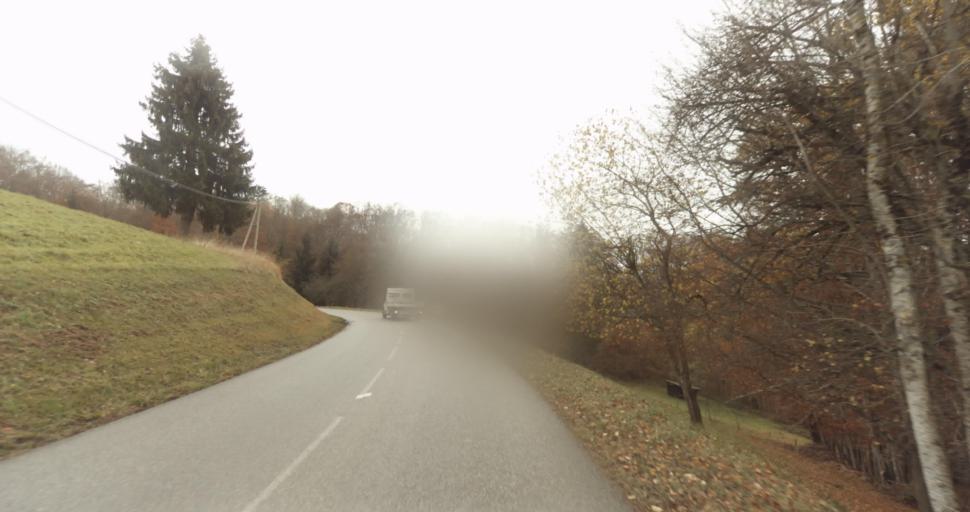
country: FR
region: Rhone-Alpes
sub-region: Departement de la Haute-Savoie
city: Thorens-Glieres
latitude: 46.0191
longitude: 6.2477
